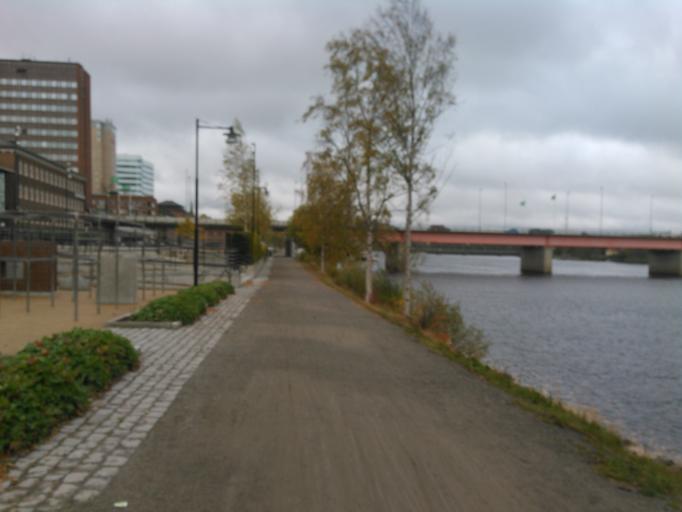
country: SE
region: Vaesterbotten
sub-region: Umea Kommun
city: Umea
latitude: 63.8258
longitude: 20.2524
